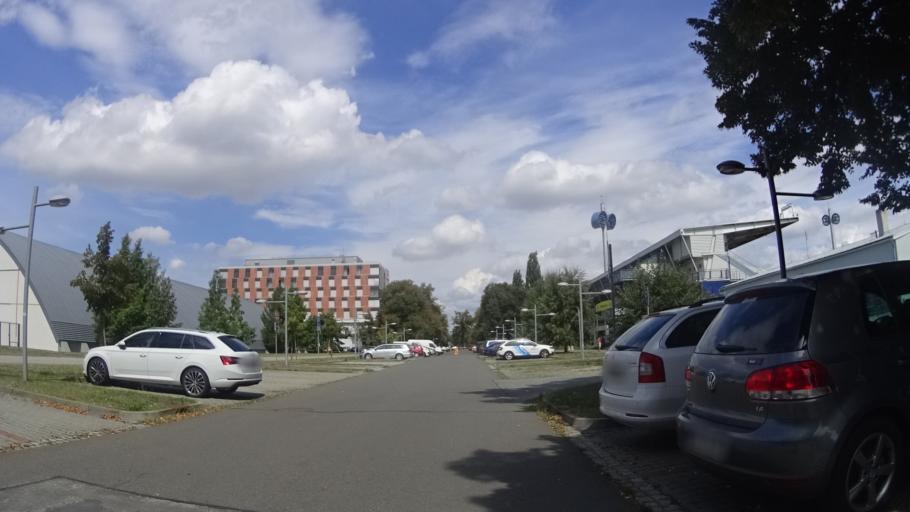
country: CZ
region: Olomoucky
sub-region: Okres Olomouc
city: Olomouc
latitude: 49.5995
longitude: 17.2467
